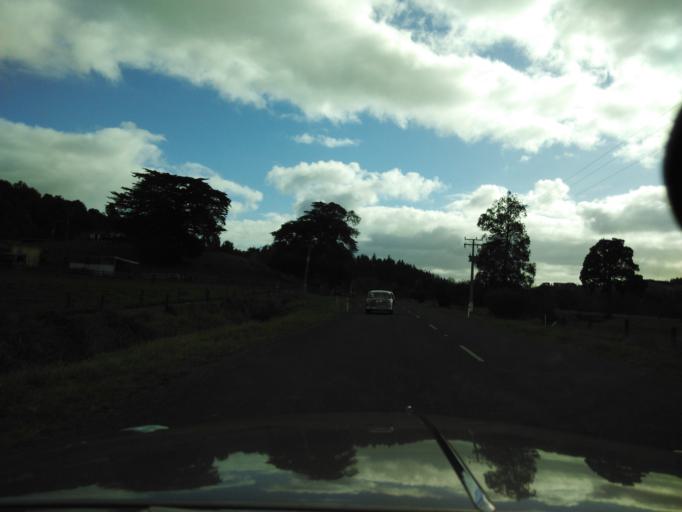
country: NZ
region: Auckland
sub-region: Auckland
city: Red Hill
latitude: -37.0986
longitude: 175.0942
